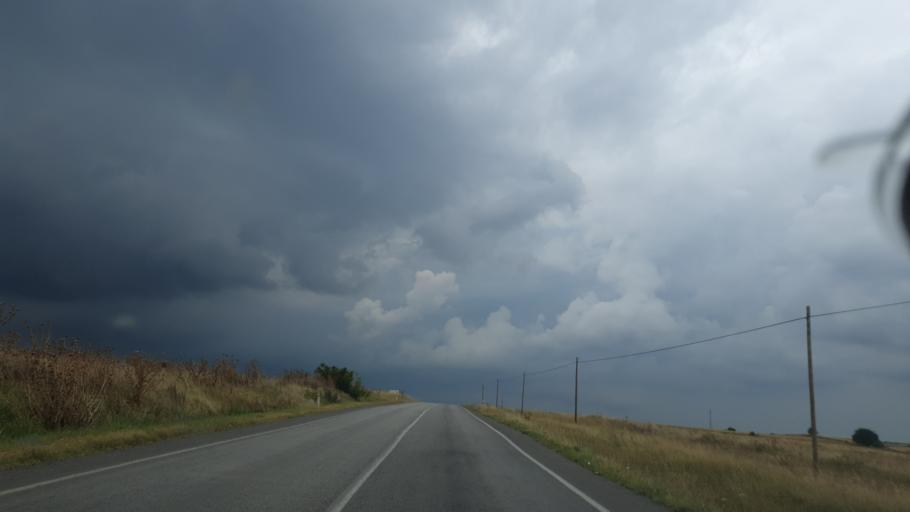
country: TR
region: Tekirdag
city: Hayrabolu
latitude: 41.2190
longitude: 27.0556
